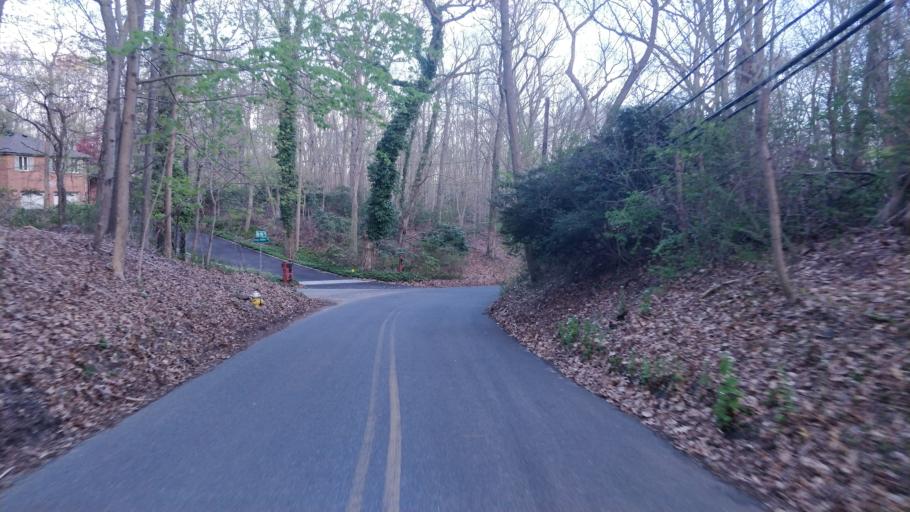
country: US
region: New York
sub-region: Suffolk County
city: Nissequogue
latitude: 40.8845
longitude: -73.1853
